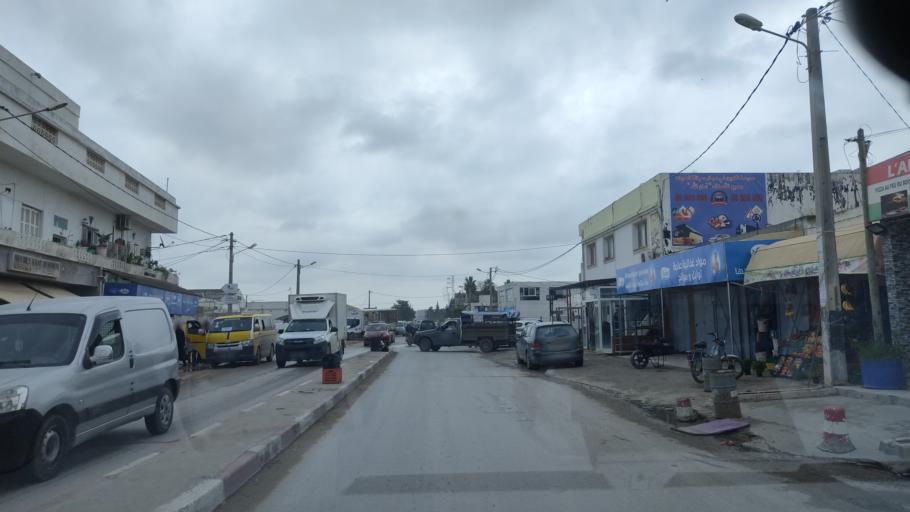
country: TN
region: Ariana
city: Ariana
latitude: 36.8861
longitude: 10.2185
